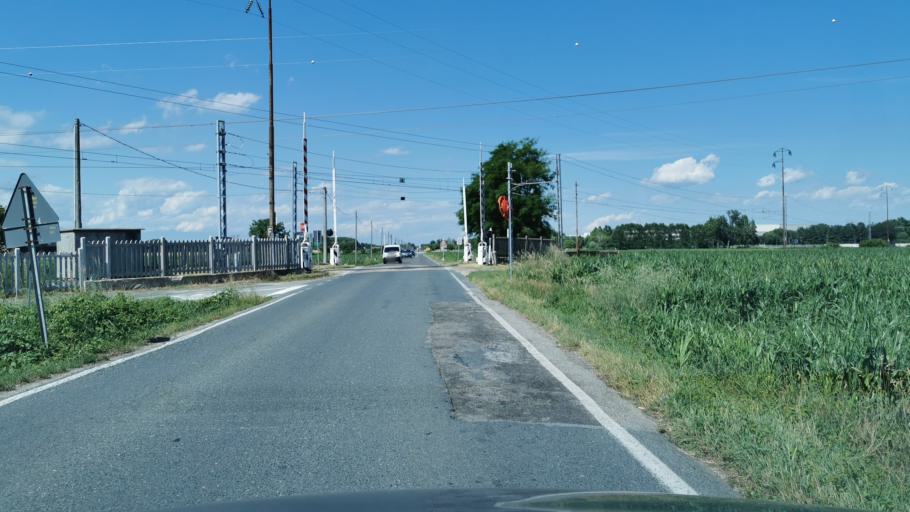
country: IT
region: Piedmont
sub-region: Provincia di Torino
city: Airasca
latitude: 44.9321
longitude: 7.5012
